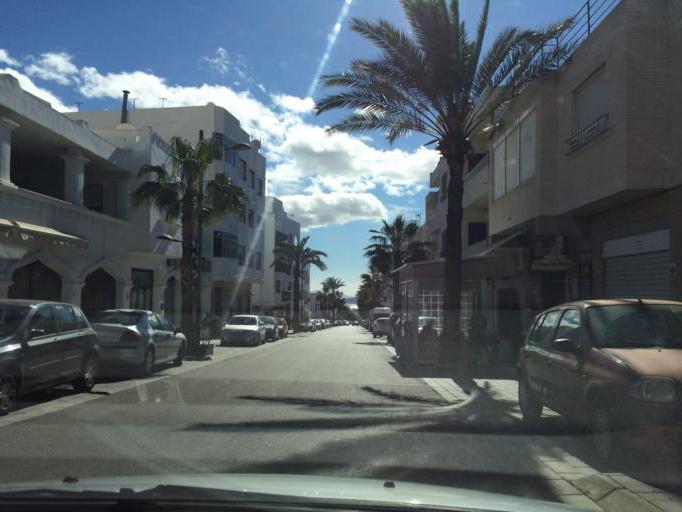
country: ES
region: Andalusia
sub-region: Provincia de Almeria
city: Nijar
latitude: 36.9641
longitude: -2.2076
